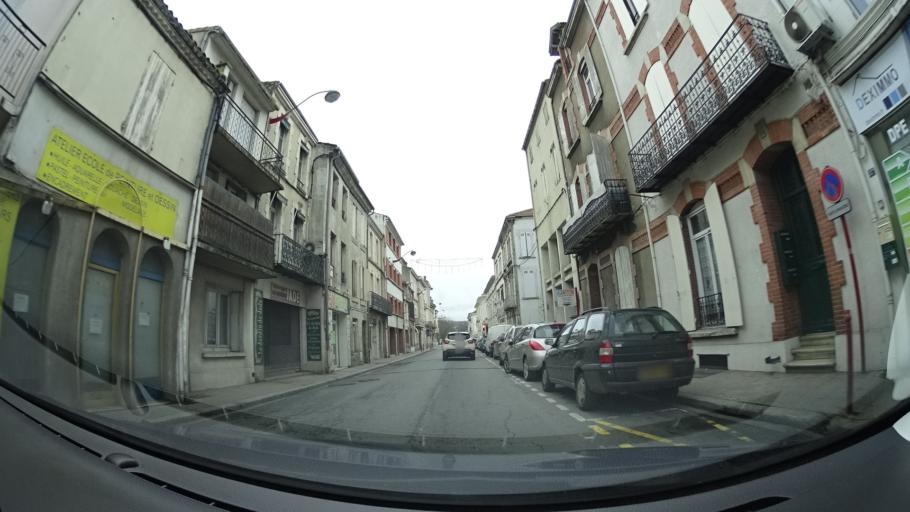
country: FR
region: Aquitaine
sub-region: Departement du Lot-et-Garonne
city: Villeneuve-sur-Lot
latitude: 44.4085
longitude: 0.7040
